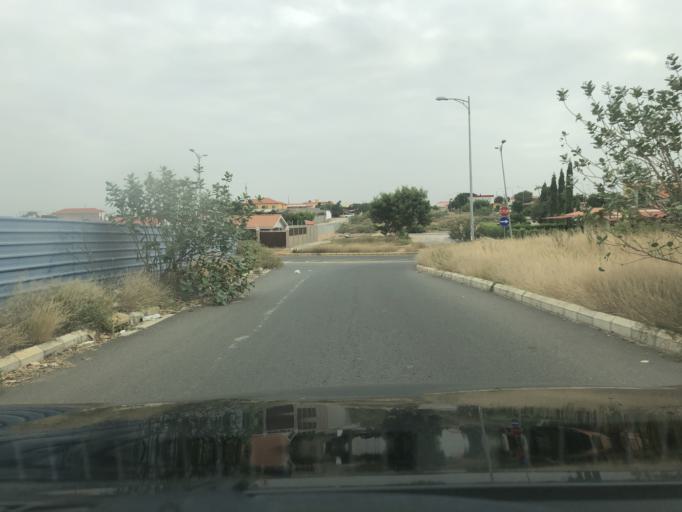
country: AO
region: Luanda
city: Luanda
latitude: -8.9460
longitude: 13.2493
